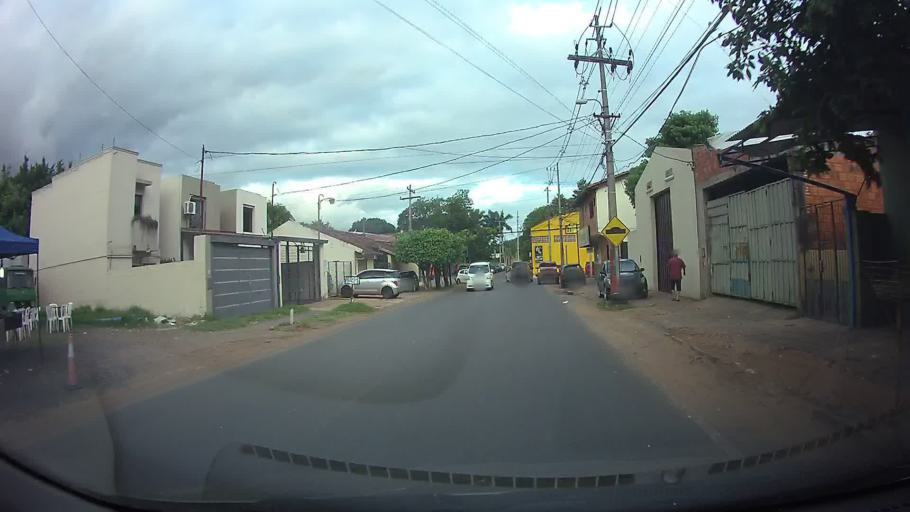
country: PY
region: Central
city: Fernando de la Mora
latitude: -25.3185
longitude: -57.5387
